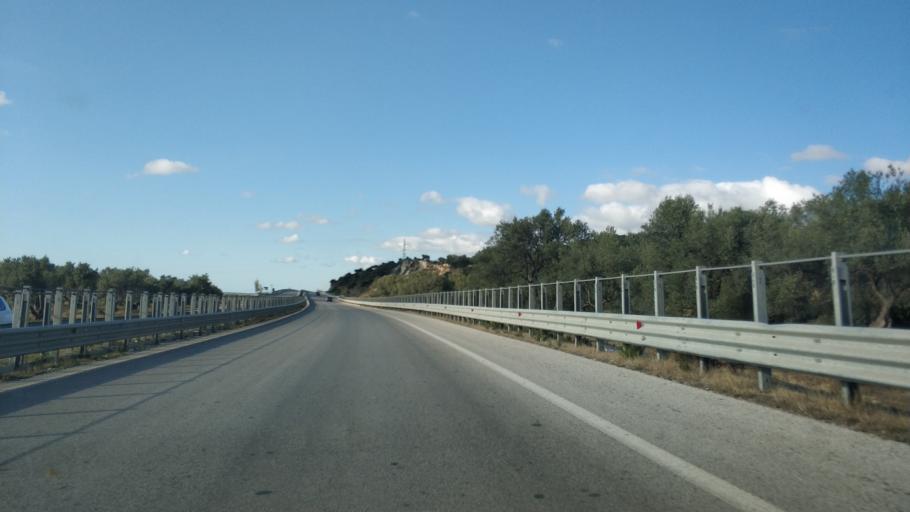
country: AL
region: Vlore
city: Vlore
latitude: 40.5073
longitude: 19.4630
